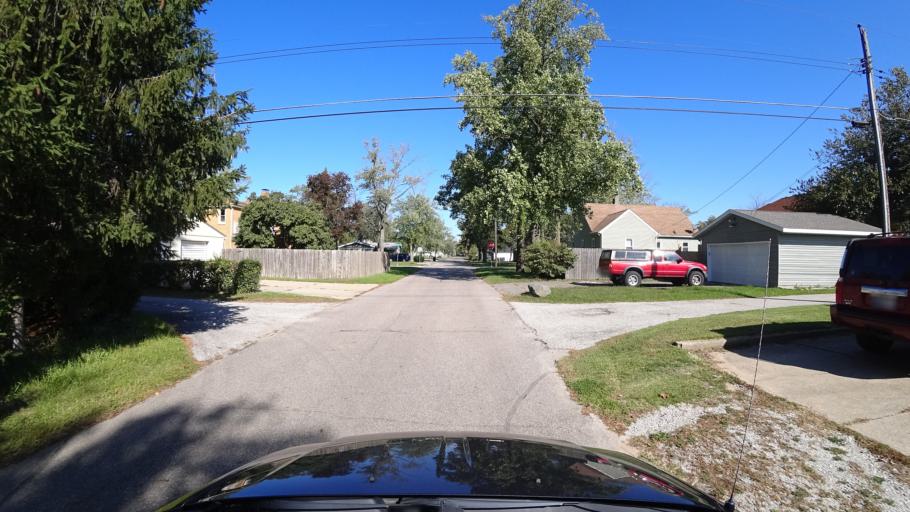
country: US
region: Indiana
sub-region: LaPorte County
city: Michigan City
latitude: 41.7086
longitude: -86.8878
